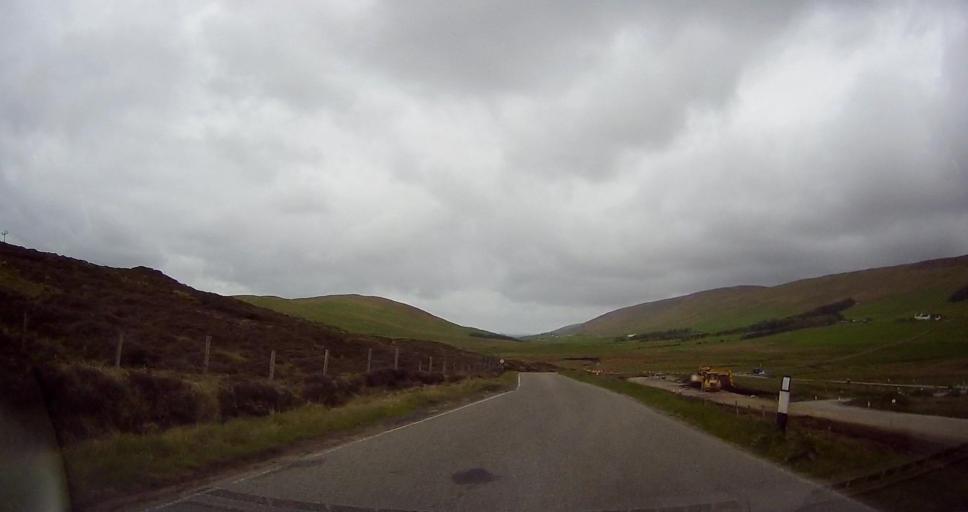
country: GB
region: Scotland
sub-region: Shetland Islands
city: Lerwick
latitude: 60.2776
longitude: -1.2717
